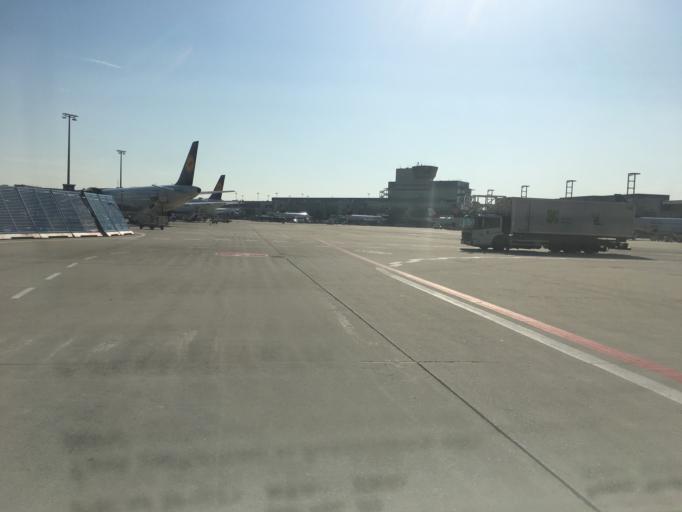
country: DE
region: Hesse
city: Kelsterbach
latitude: 50.0446
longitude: 8.5598
